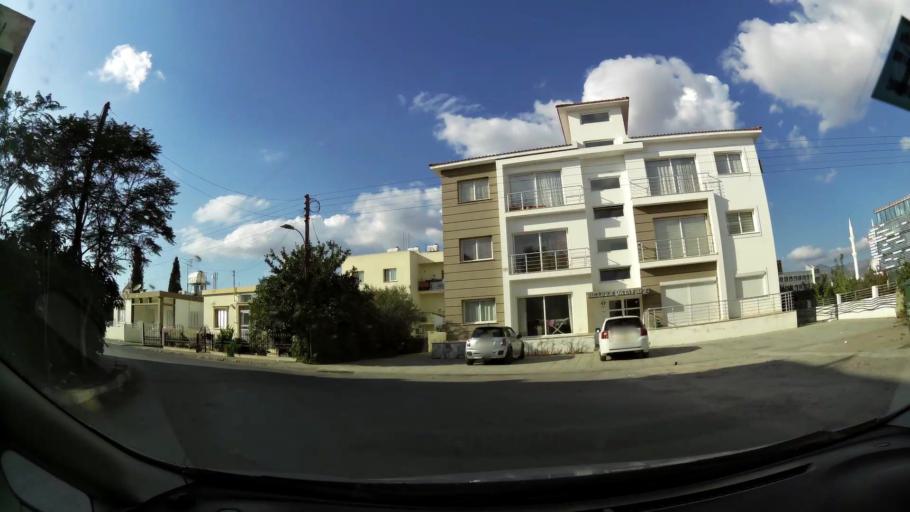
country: CY
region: Lefkosia
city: Nicosia
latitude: 35.2002
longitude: 33.3625
